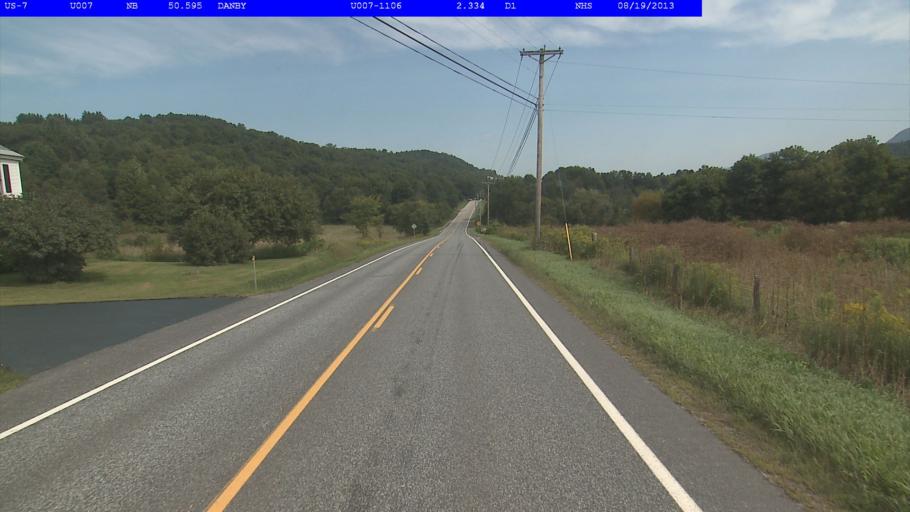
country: US
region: Vermont
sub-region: Rutland County
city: West Rutland
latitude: 43.3954
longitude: -72.9989
